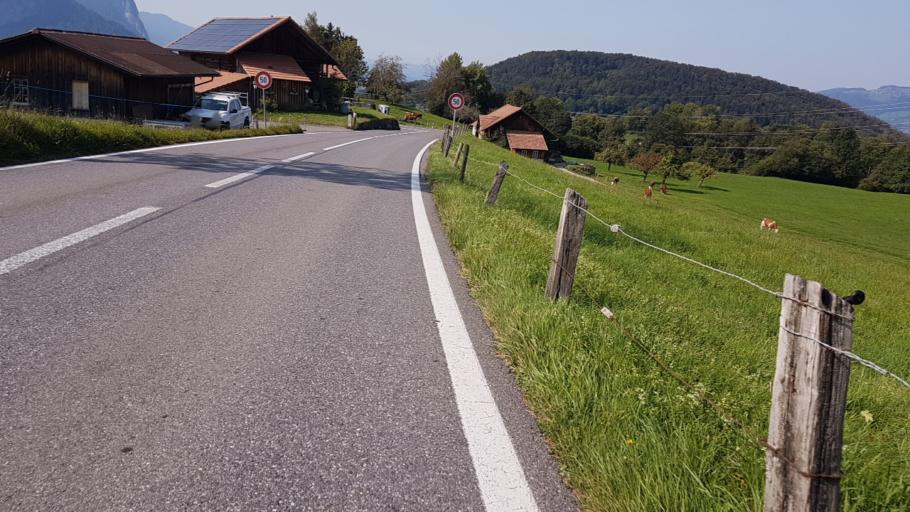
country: CH
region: Bern
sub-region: Frutigen-Niedersimmental District
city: Aeschi
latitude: 46.6642
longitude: 7.6876
